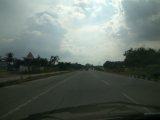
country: IN
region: Karnataka
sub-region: Kolar
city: Malur
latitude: 13.1306
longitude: 77.9639
